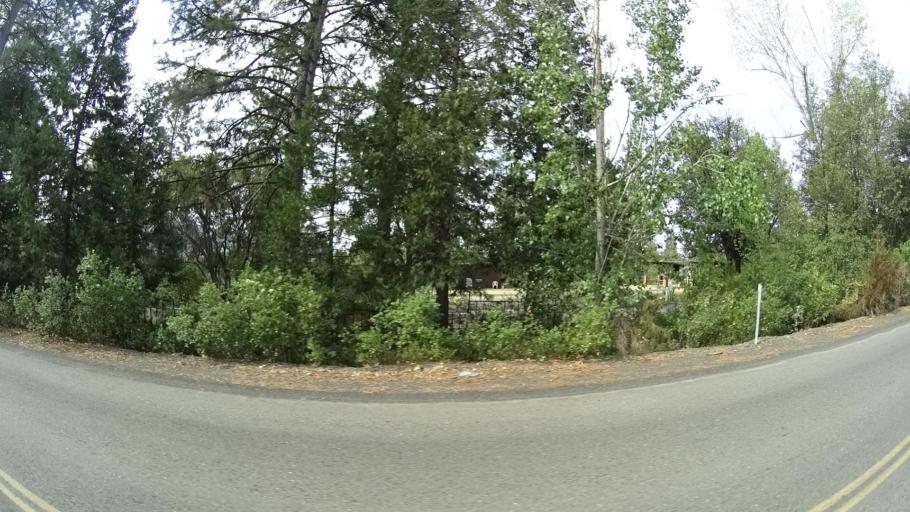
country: US
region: California
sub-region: Madera County
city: Ahwahnee
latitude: 37.4679
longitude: -119.7678
